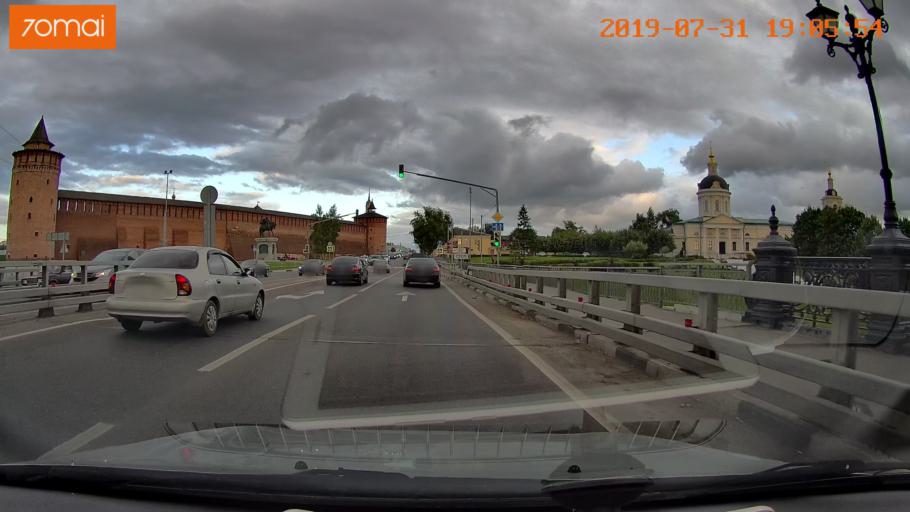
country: RU
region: Moskovskaya
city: Kolomna
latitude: 55.1044
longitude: 38.7491
